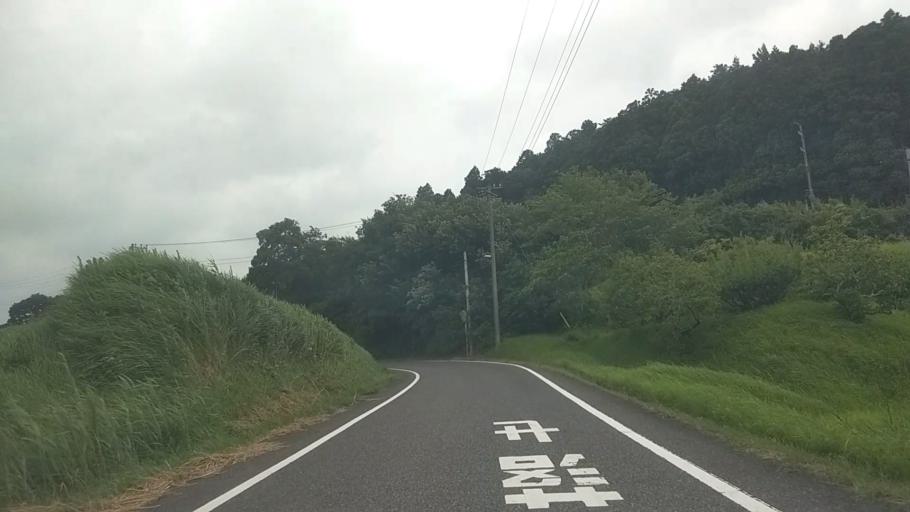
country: JP
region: Chiba
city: Kawaguchi
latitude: 35.2620
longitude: 140.0577
